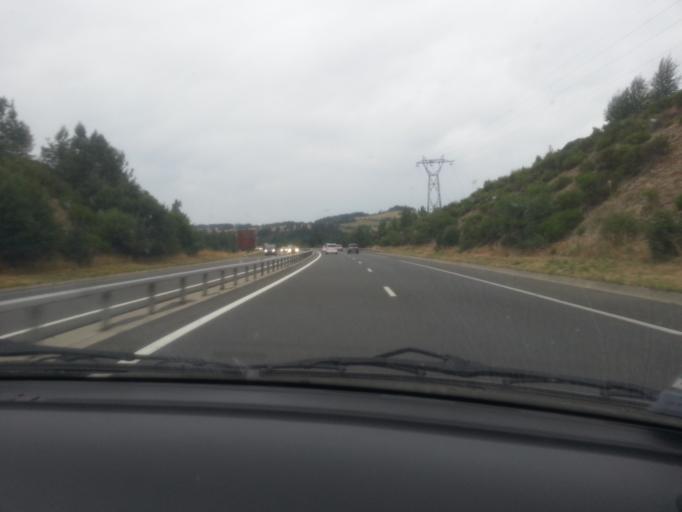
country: FR
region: Languedoc-Roussillon
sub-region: Departement de la Lozere
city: Marvejols
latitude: 44.6107
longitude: 3.2582
